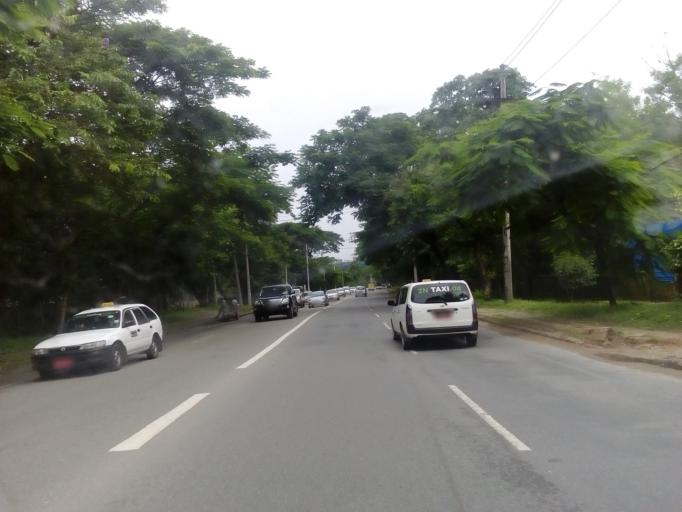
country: MM
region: Yangon
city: Yangon
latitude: 16.8561
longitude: 96.1334
